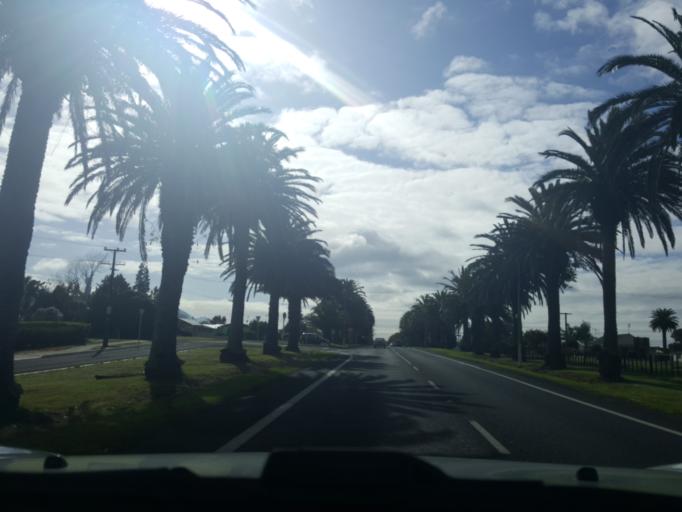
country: NZ
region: Waikato
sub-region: Hauraki District
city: Waihi
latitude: -37.3983
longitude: 175.8262
